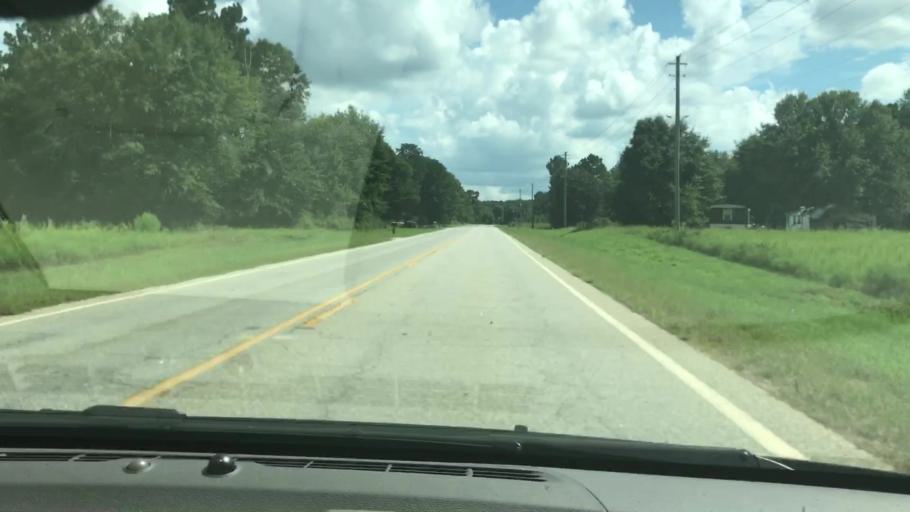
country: US
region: Georgia
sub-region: Clay County
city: Fort Gaines
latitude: 31.6504
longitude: -85.0463
